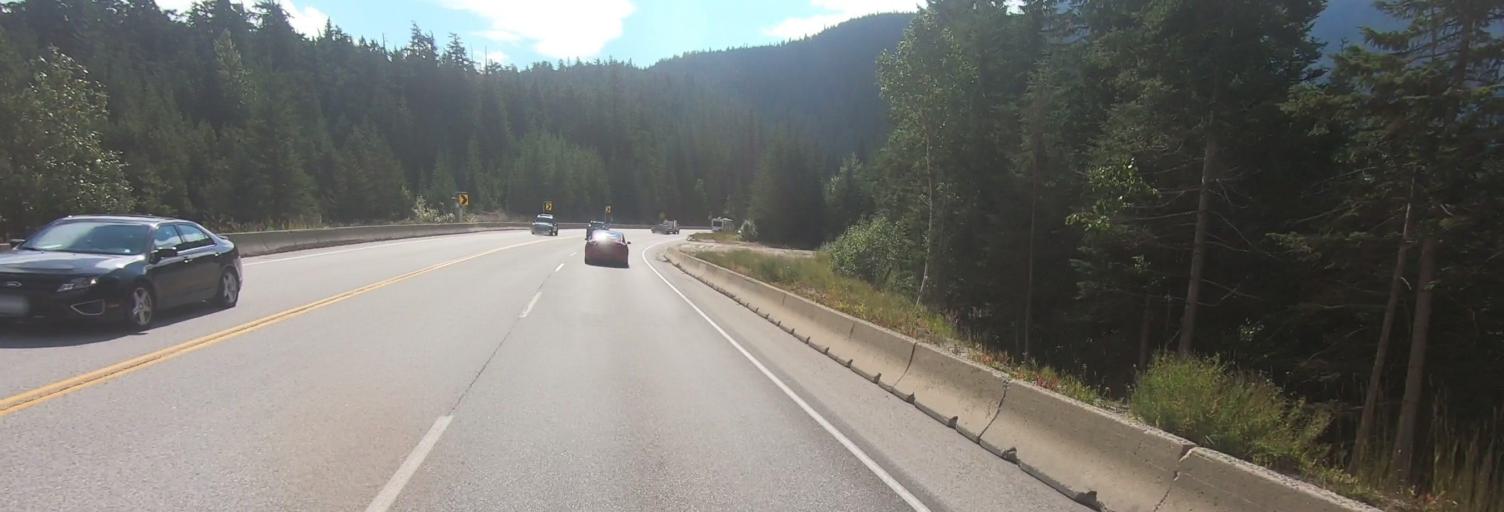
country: CA
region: British Columbia
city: Golden
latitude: 51.3473
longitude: -117.4351
